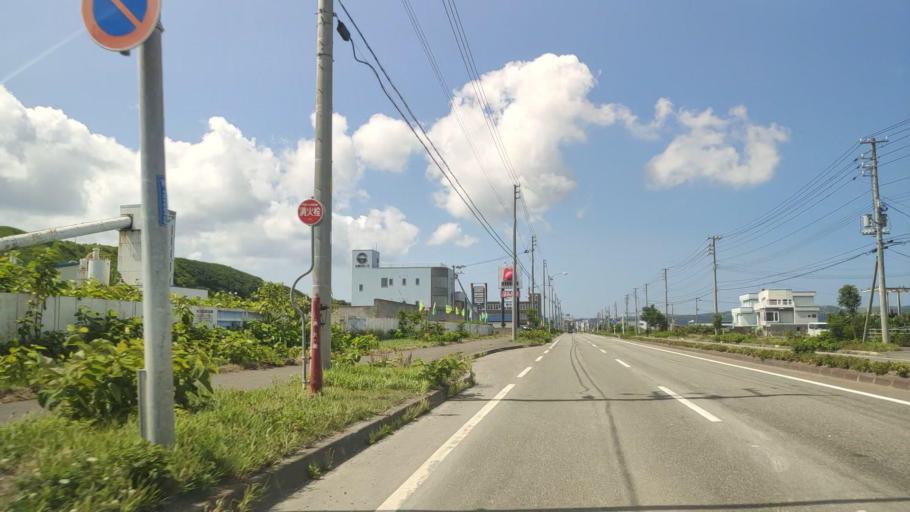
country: JP
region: Hokkaido
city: Wakkanai
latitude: 45.3969
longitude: 141.7303
